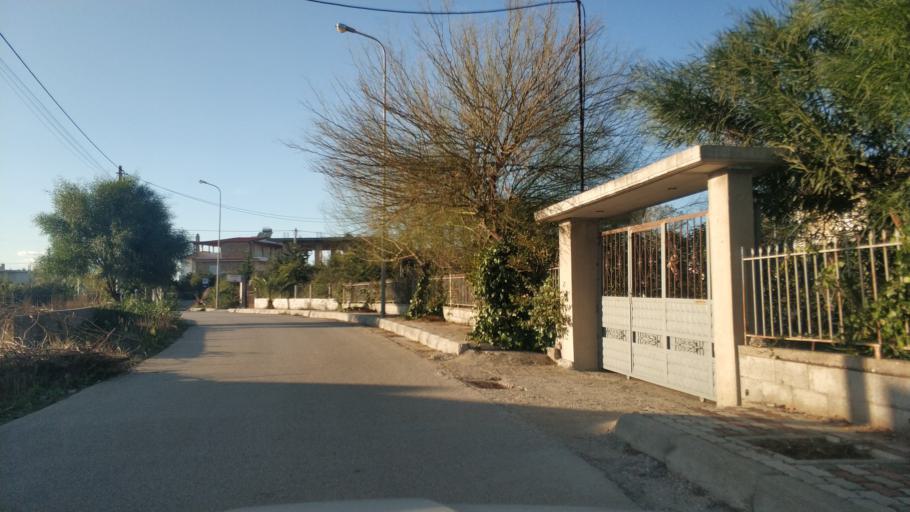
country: AL
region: Vlore
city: Vlore
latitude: 40.5061
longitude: 19.4140
